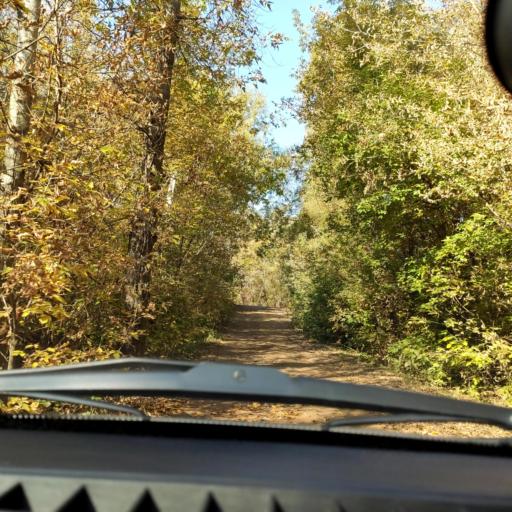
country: RU
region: Bashkortostan
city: Ufa
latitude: 54.6786
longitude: 55.9785
